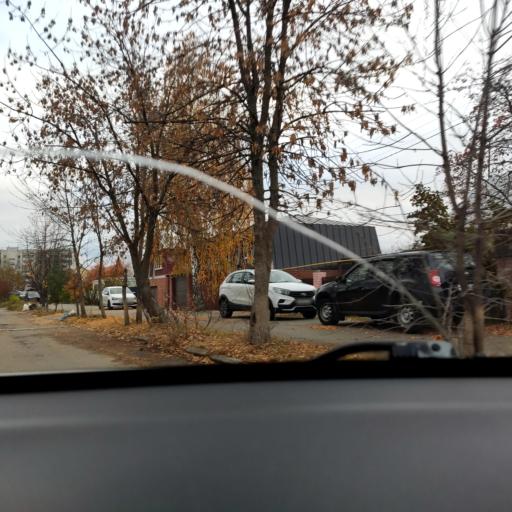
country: RU
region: Tatarstan
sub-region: Gorod Kazan'
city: Kazan
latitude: 55.8416
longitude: 49.1184
